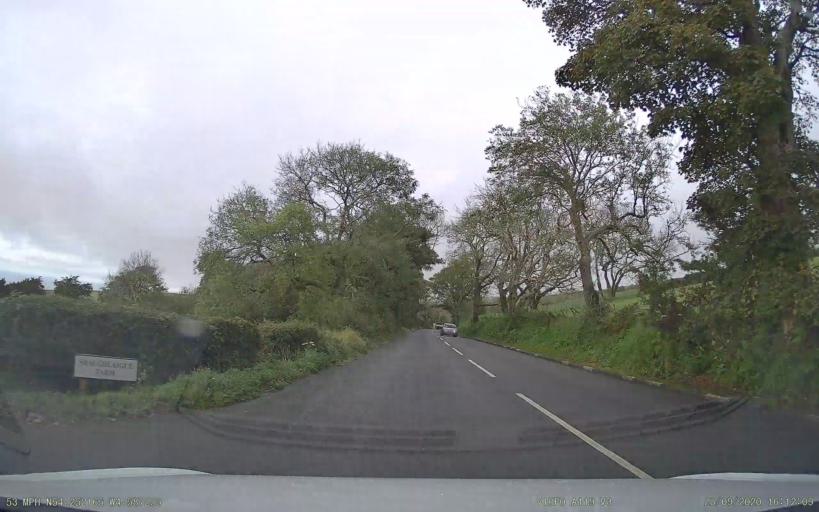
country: IM
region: Douglas
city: Douglas
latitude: 54.2522
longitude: -4.5873
